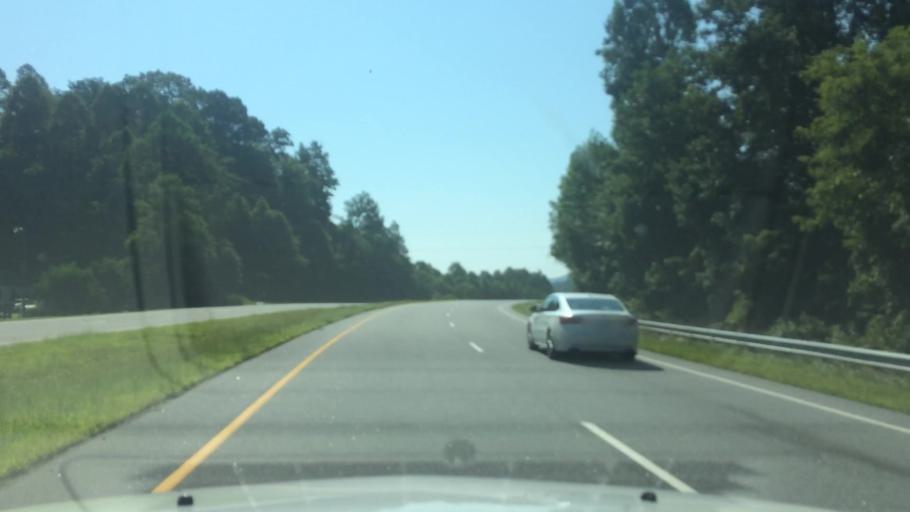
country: US
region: North Carolina
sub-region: Caldwell County
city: Lenoir
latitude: 35.9568
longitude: -81.5607
